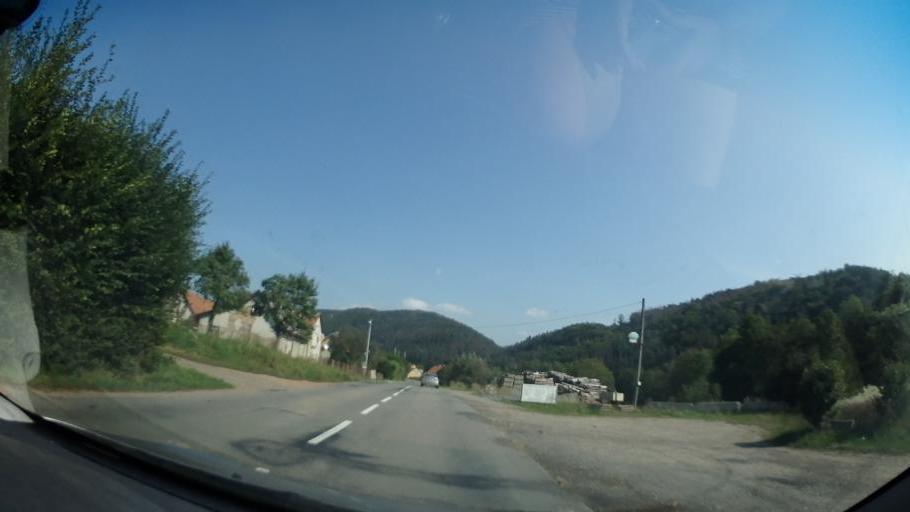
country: CZ
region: South Moravian
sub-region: Okres Brno-Venkov
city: Nedvedice
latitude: 49.4403
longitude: 16.3445
